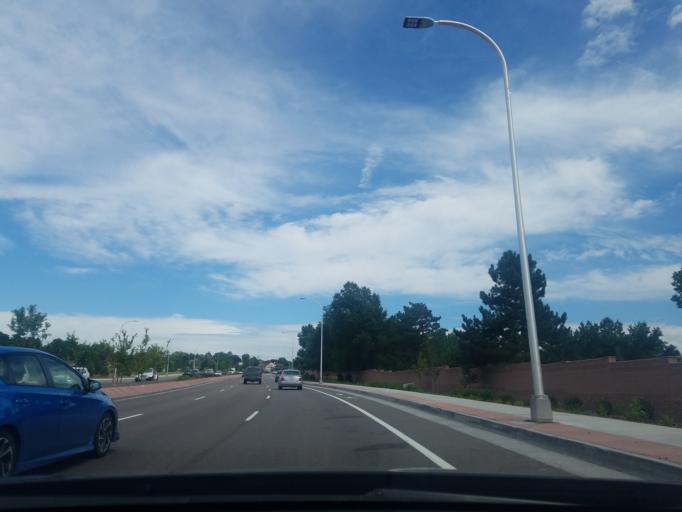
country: US
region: Colorado
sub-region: El Paso County
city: Air Force Academy
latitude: 38.9325
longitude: -104.7883
